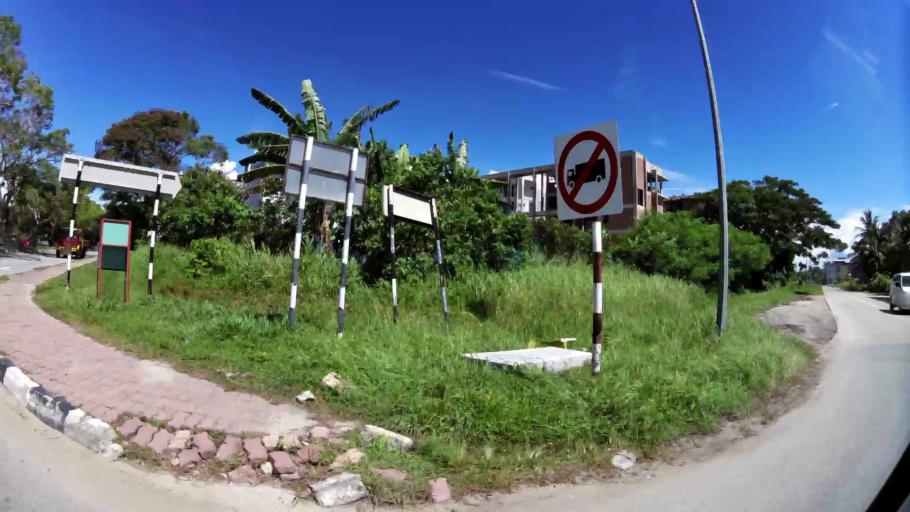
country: BN
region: Brunei and Muara
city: Bandar Seri Begawan
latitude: 5.0293
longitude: 115.0627
